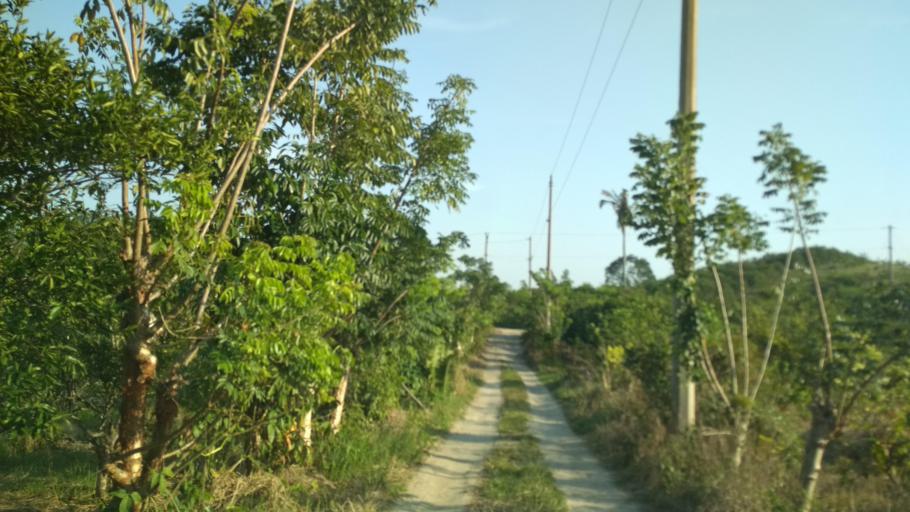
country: MX
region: Puebla
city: San Jose Acateno
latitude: 20.2278
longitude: -97.2605
